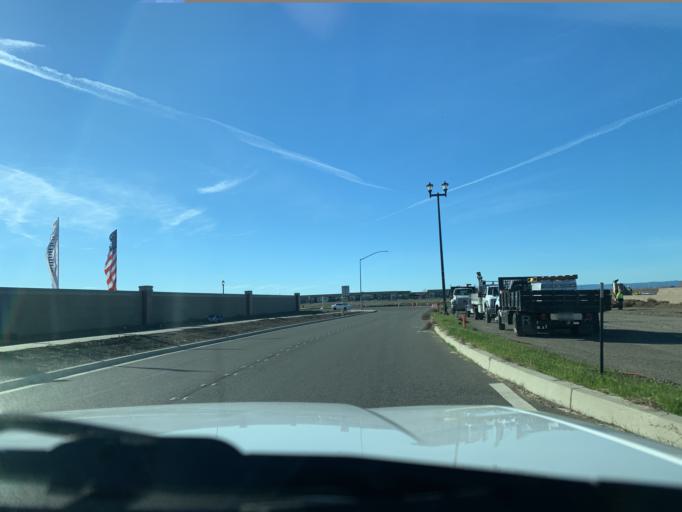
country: US
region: California
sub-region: Yolo County
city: Woodland
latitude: 38.6516
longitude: -121.7429
